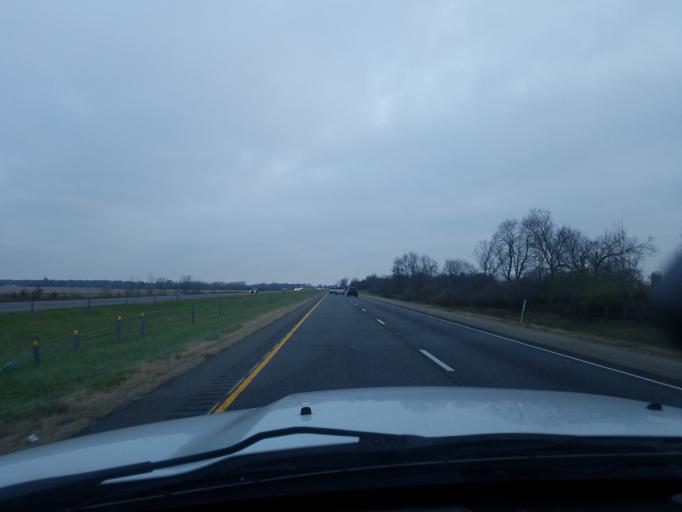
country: US
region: Indiana
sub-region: Delaware County
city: Daleville
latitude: 40.1570
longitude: -85.5668
